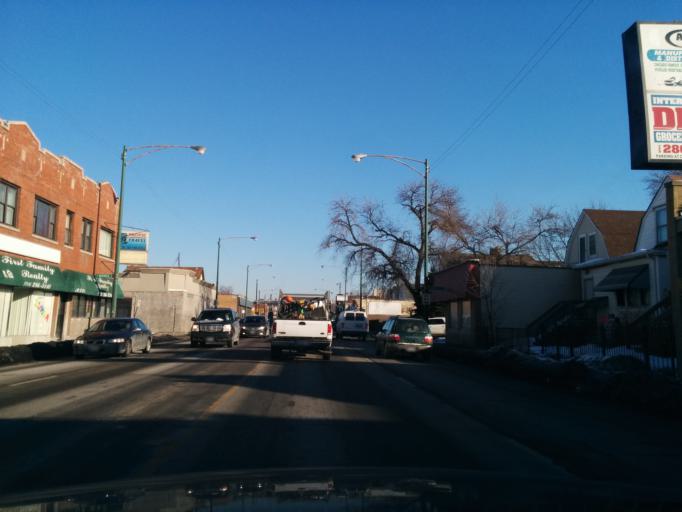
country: US
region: Illinois
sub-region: Cook County
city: Lincolnwood
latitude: 41.9482
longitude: -87.7471
